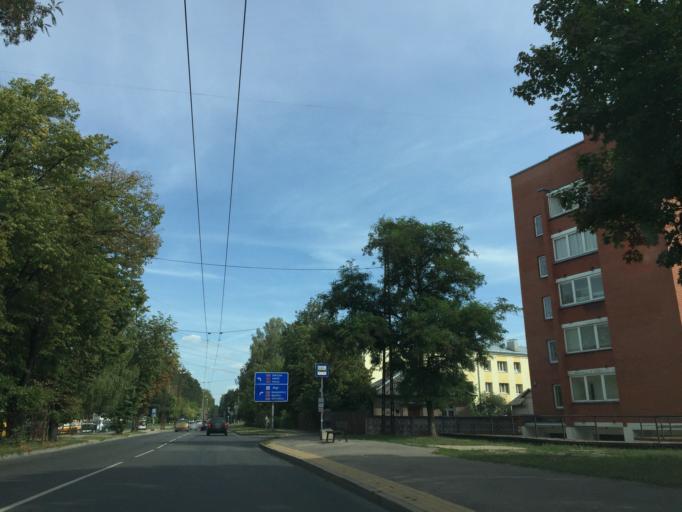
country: LV
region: Riga
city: Jaunciems
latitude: 56.9682
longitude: 24.1934
